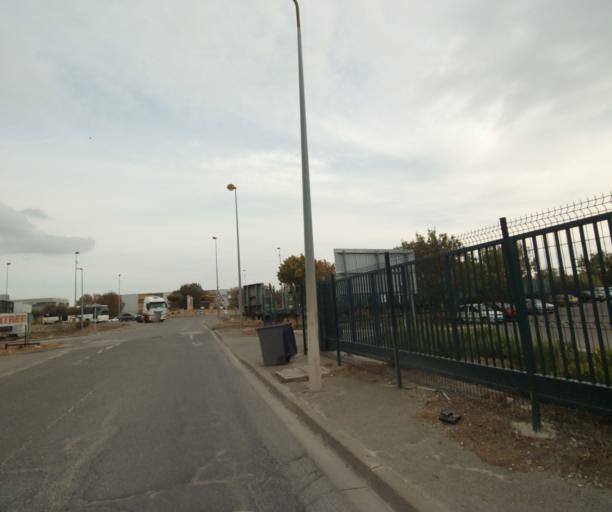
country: FR
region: Provence-Alpes-Cote d'Azur
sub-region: Departement des Bouches-du-Rhone
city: Marignane
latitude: 43.4057
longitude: 5.2034
